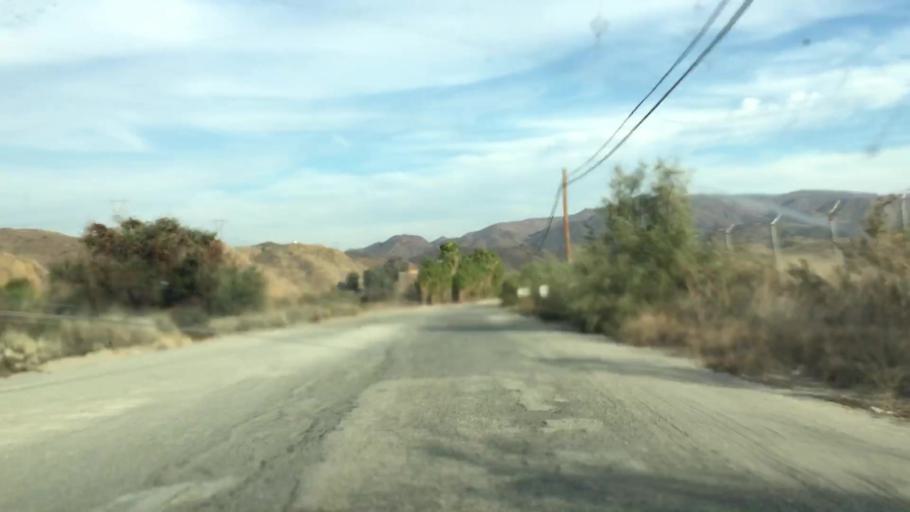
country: US
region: California
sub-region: Riverside County
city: El Cerrito
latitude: 33.7826
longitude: -117.4829
